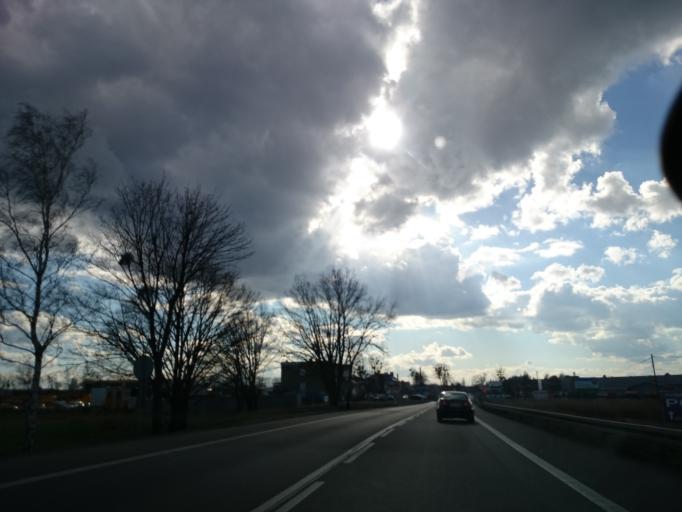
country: PL
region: Opole Voivodeship
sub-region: Powiat opolski
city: Niemodlin
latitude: 50.6465
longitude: 17.6484
